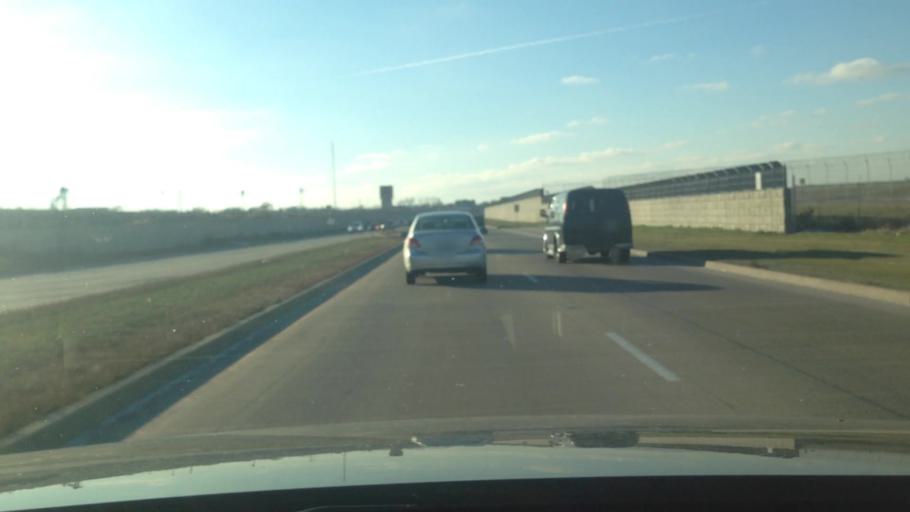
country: US
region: Illinois
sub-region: DuPage County
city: Bensenville
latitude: 41.9553
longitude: -87.9222
